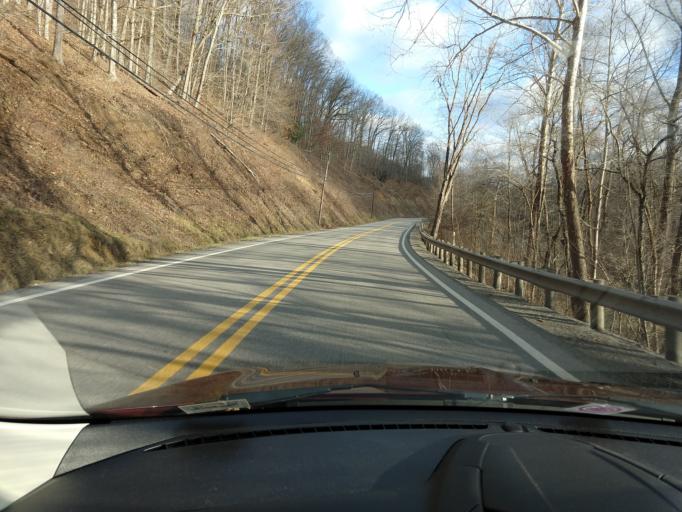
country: US
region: West Virginia
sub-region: Randolph County
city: Elkins
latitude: 38.7587
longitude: -79.9537
